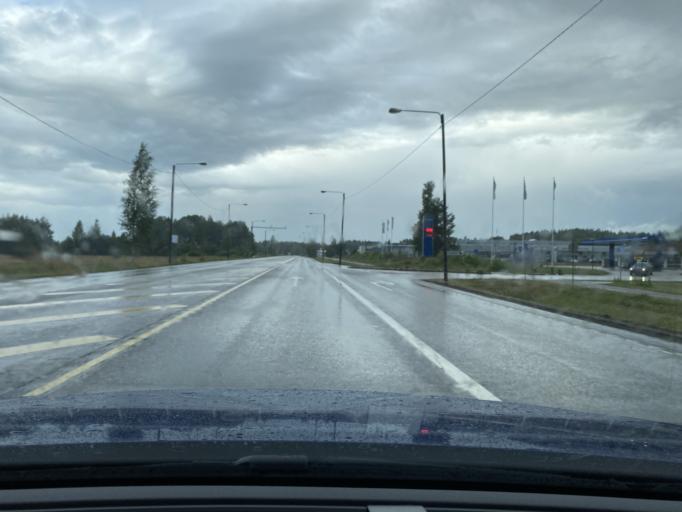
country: FI
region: Uusimaa
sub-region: Helsinki
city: Hyvinge
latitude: 60.6089
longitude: 24.8062
